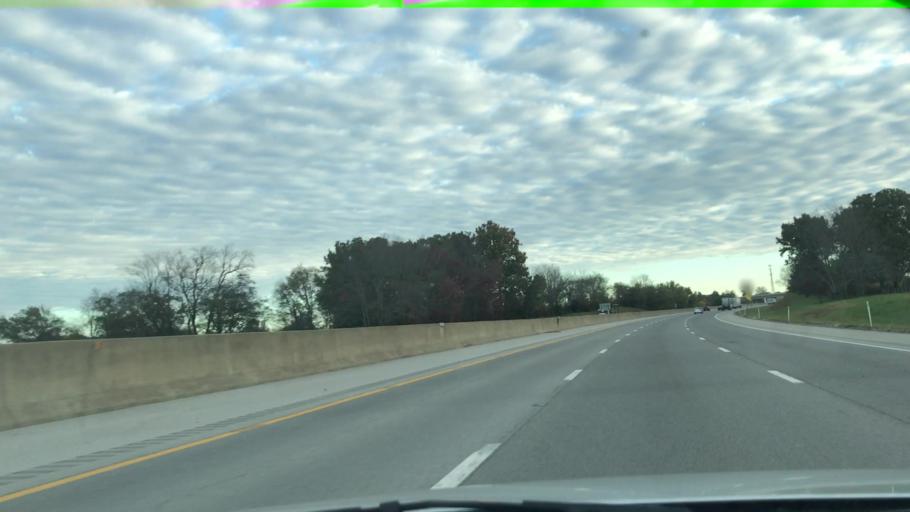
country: US
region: Kentucky
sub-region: Simpson County
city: Franklin
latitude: 36.7318
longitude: -86.5131
